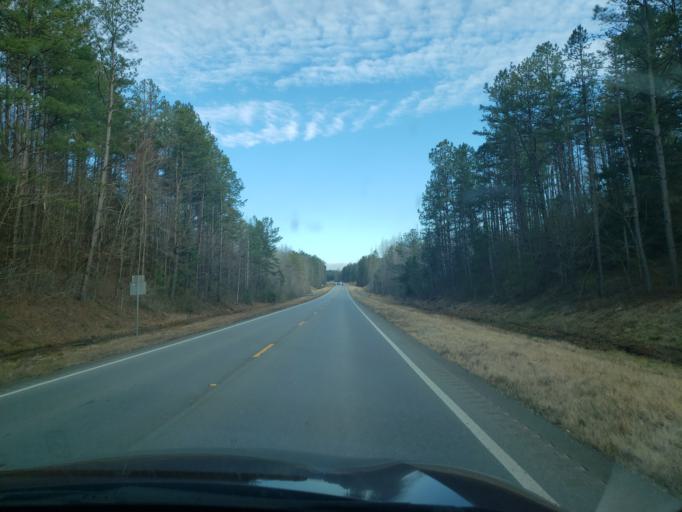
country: US
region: Alabama
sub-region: Randolph County
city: Wedowee
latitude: 33.4306
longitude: -85.5549
